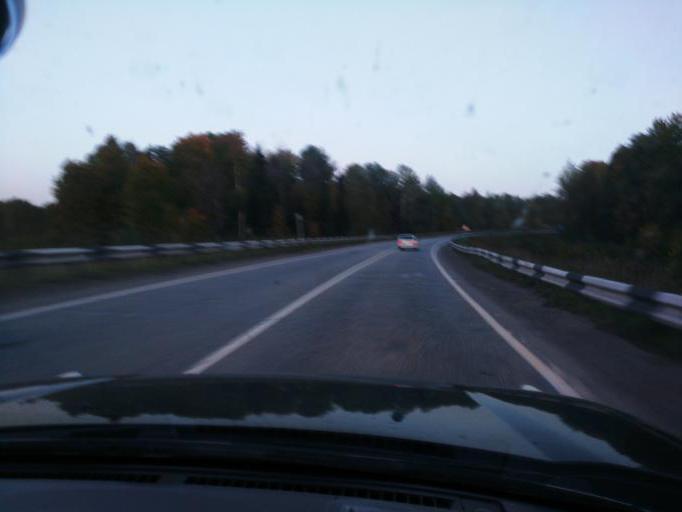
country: RU
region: Perm
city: Verkhnechusovskiye Gorodki
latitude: 58.2929
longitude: 56.8931
